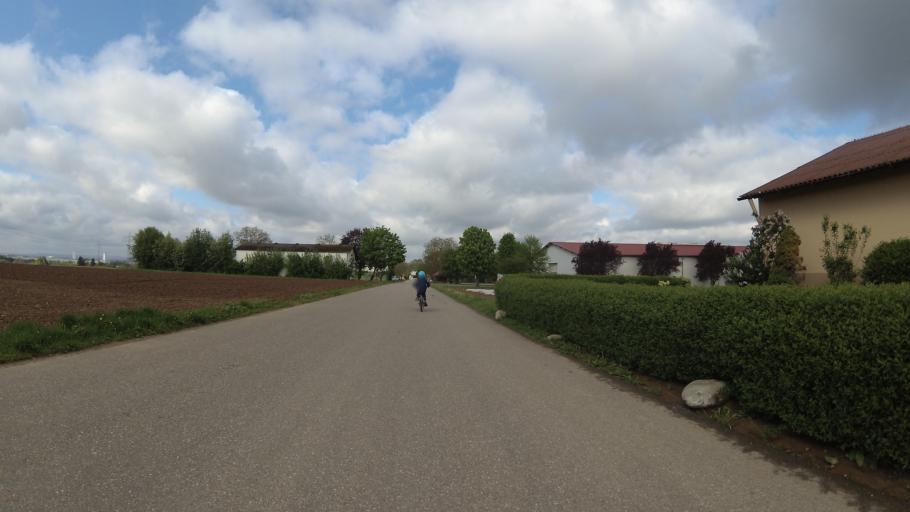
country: DE
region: Baden-Wuerttemberg
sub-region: Regierungsbezirk Stuttgart
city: Oedheim
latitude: 49.2195
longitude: 9.2355
